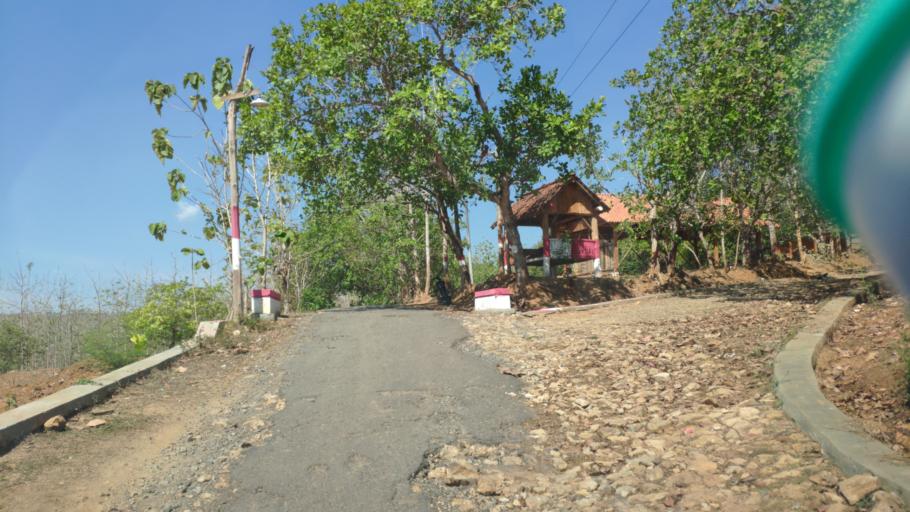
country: ID
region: East Java
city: Krajan Jamprong
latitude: -6.9952
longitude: 111.6055
